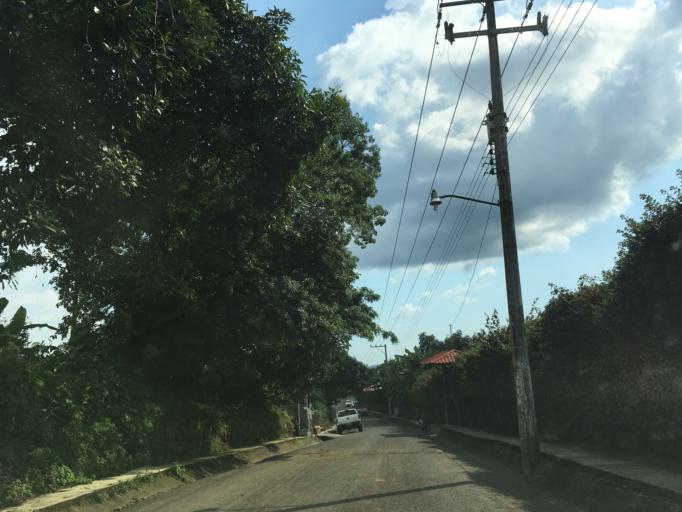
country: MX
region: Michoacan
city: Tingambato
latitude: 19.4485
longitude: -101.8676
